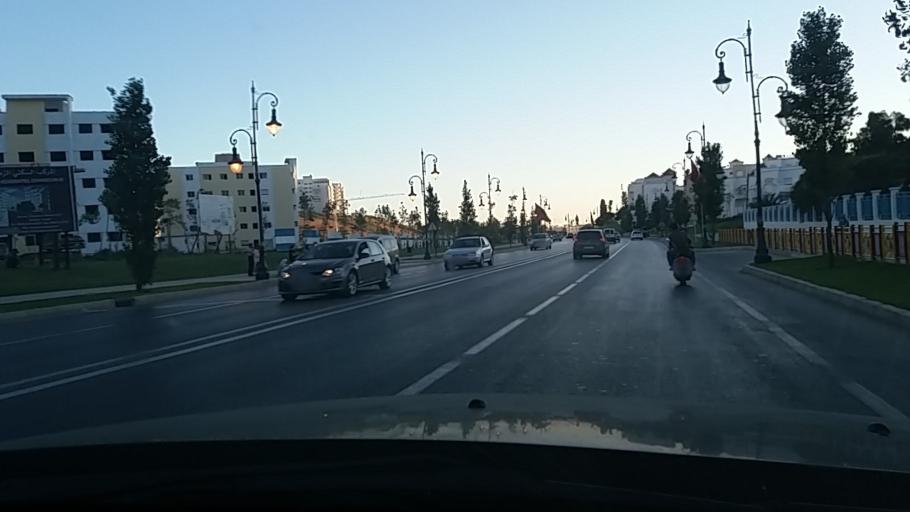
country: MA
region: Tanger-Tetouan
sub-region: Tanger-Assilah
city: Boukhalef
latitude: 35.7414
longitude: -5.8684
